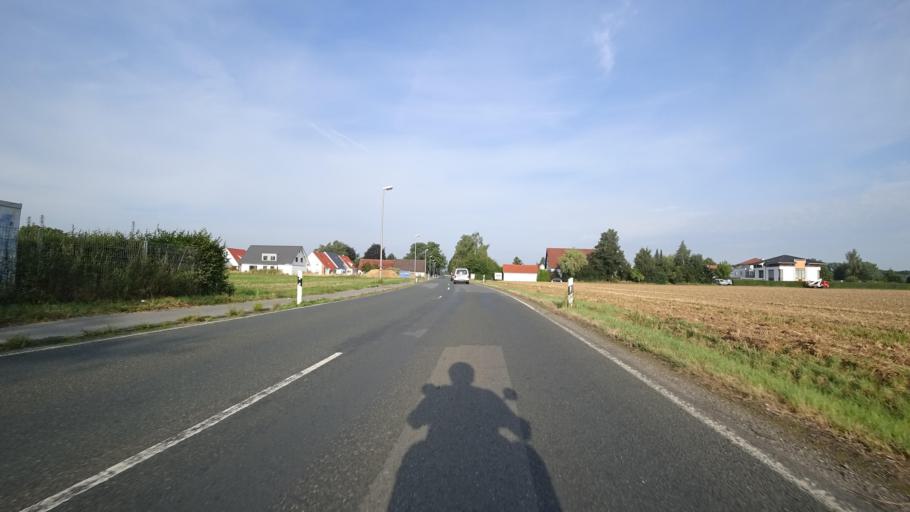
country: DE
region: North Rhine-Westphalia
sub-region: Regierungsbezirk Detmold
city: Bielefeld
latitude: 52.0593
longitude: 8.5117
